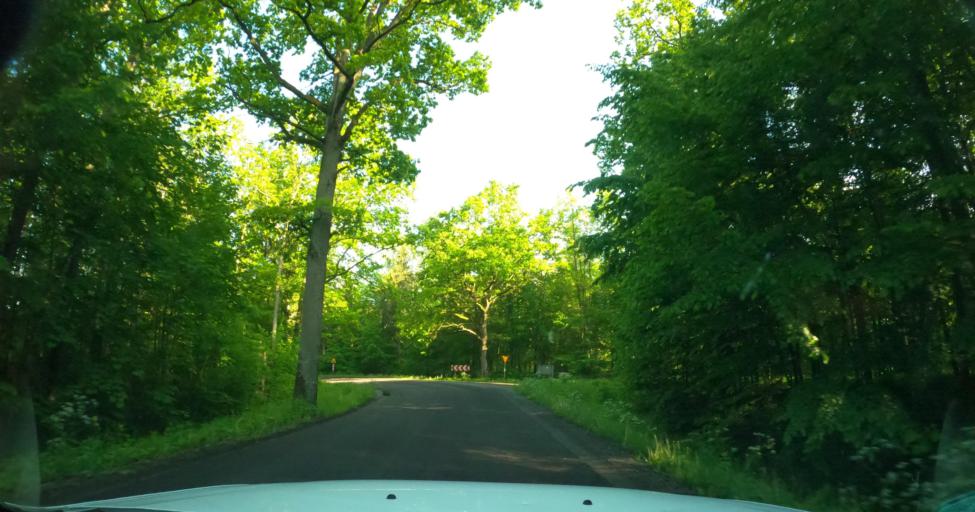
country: PL
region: Warmian-Masurian Voivodeship
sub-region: Powiat braniewski
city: Braniewo
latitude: 54.2747
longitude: 19.7947
